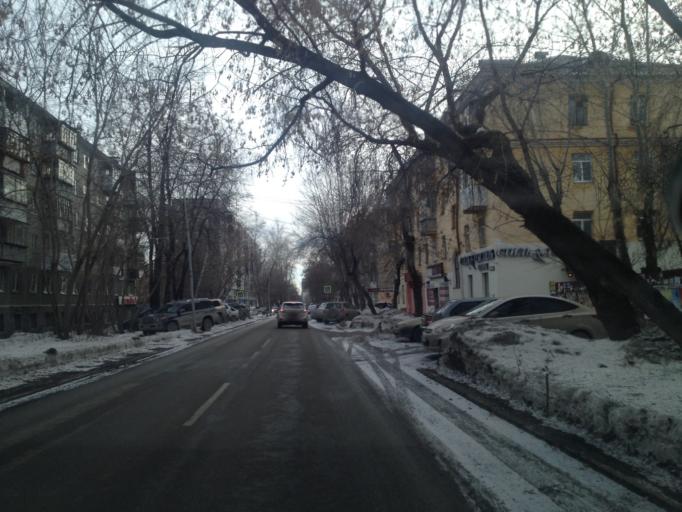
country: RU
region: Sverdlovsk
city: Yekaterinburg
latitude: 56.8127
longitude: 60.6015
